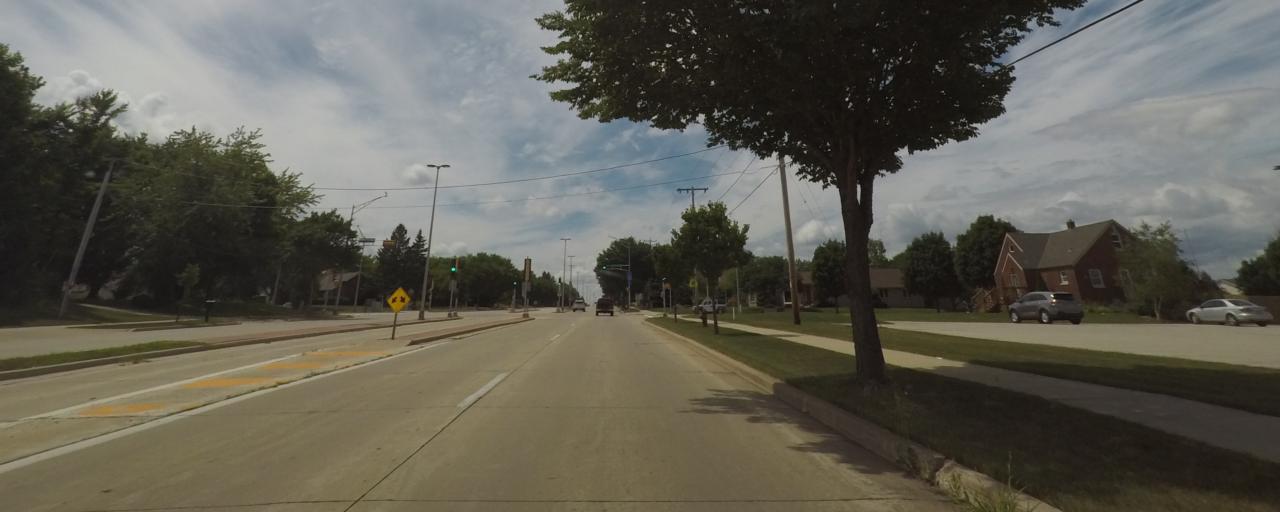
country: US
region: Wisconsin
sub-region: Milwaukee County
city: Hales Corners
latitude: 42.9592
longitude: -88.0568
